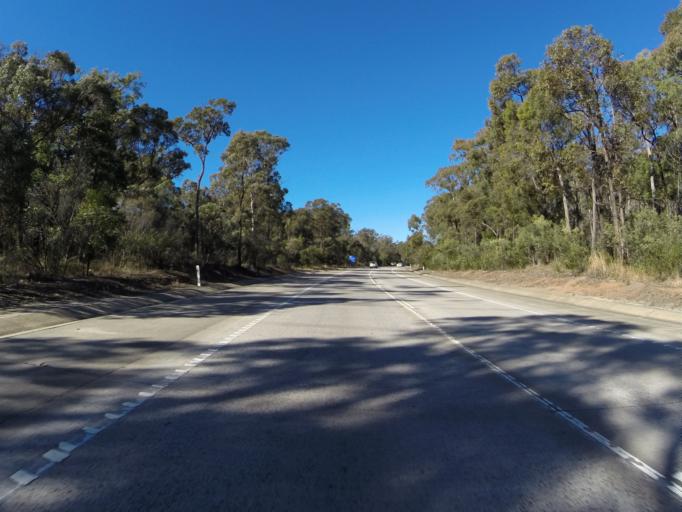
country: AU
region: New South Wales
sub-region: Wollondilly
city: Douglas Park
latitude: -34.2482
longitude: 150.7026
